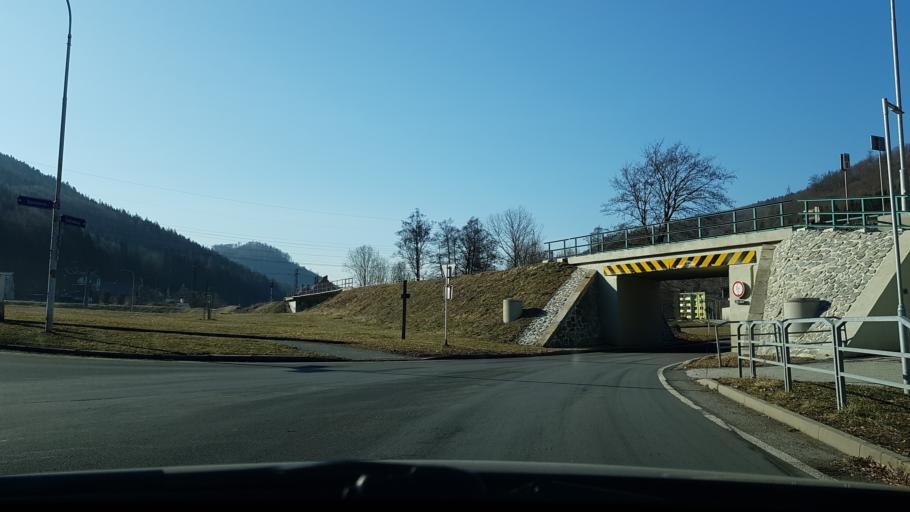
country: CZ
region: Olomoucky
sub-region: Okres Sumperk
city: Hanusovice
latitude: 50.0688
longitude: 16.9302
